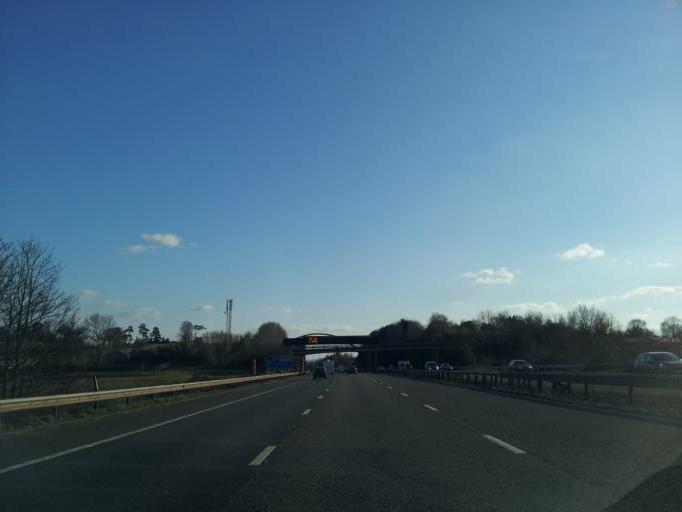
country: GB
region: England
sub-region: Devon
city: Heavitree
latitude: 50.7370
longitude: -3.4613
